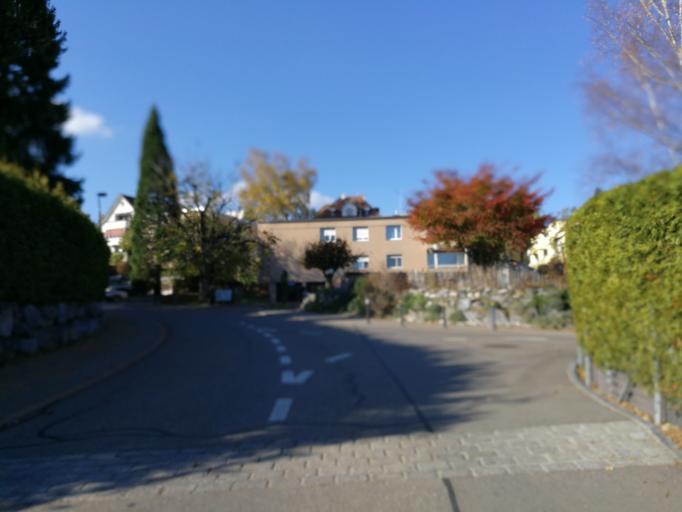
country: CH
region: Zurich
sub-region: Bezirk Uster
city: Egg
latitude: 47.3012
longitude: 8.6945
